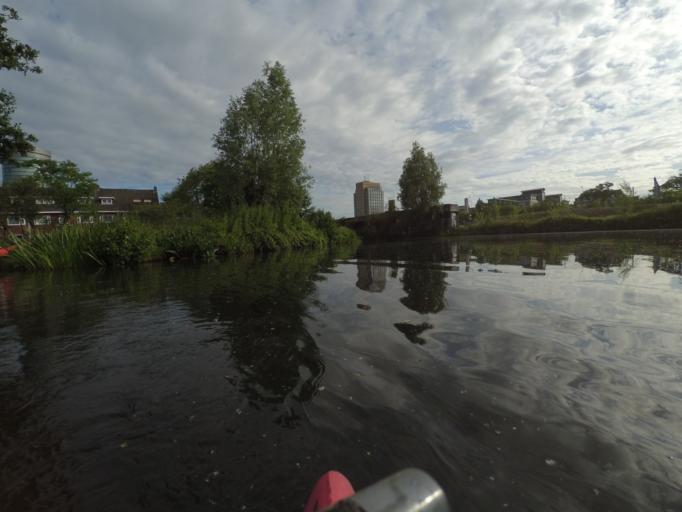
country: NL
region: Utrecht
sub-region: Gemeente Utrecht
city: Utrecht
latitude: 52.0830
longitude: 5.1131
